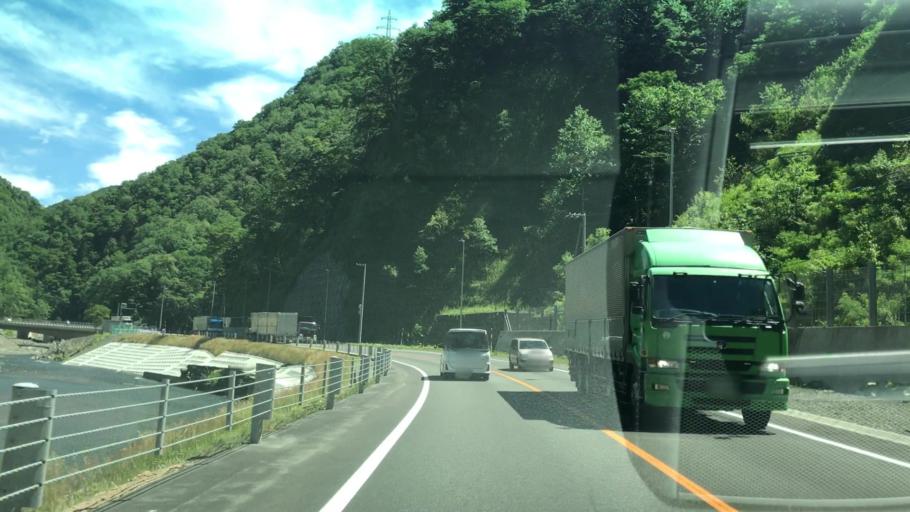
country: JP
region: Hokkaido
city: Shimo-furano
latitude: 42.9480
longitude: 142.6009
